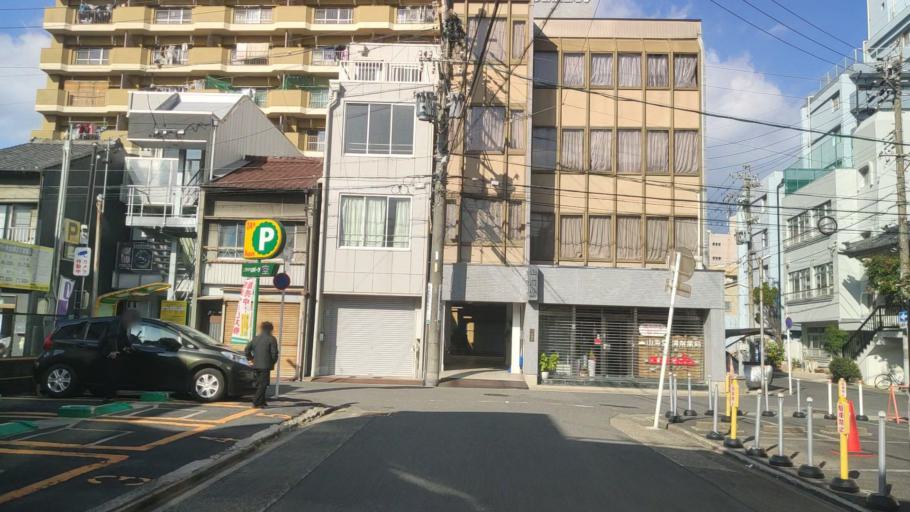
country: JP
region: Aichi
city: Nagoya-shi
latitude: 35.1584
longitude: 136.9002
